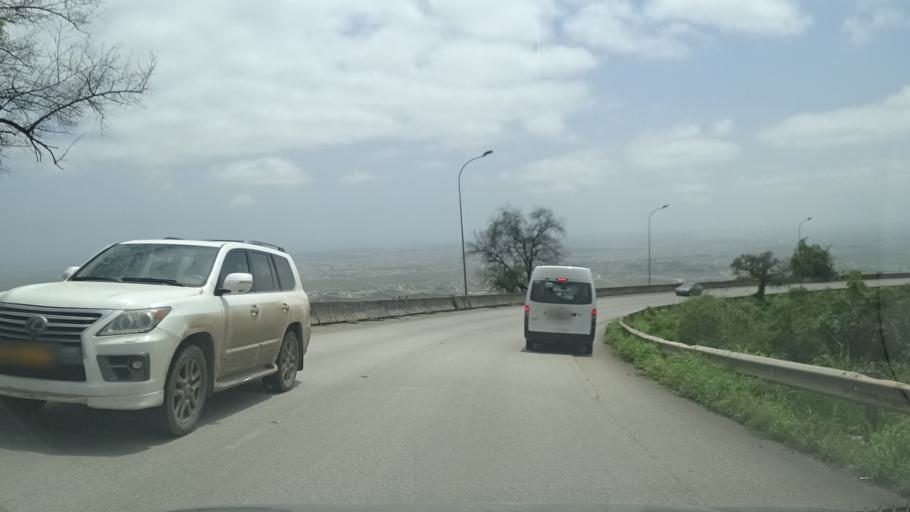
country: OM
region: Zufar
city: Salalah
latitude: 17.1524
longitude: 54.2228
